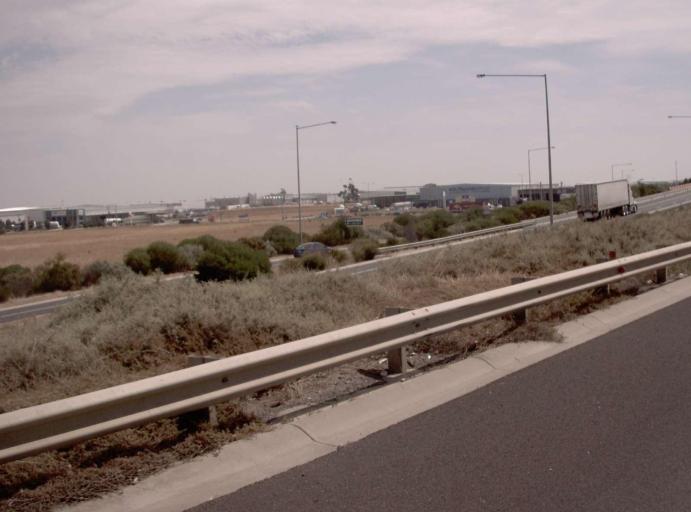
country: AU
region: Victoria
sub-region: Brimbank
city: Derrimut
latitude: -37.8000
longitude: 144.7923
